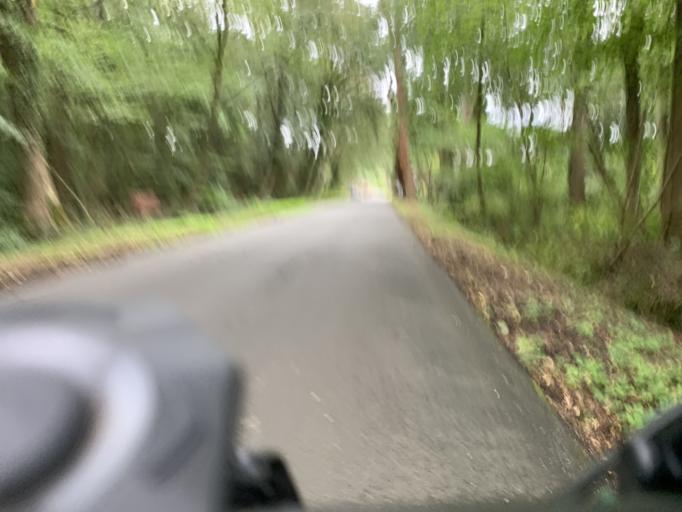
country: DE
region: Lower Saxony
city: Westerstede
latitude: 53.2349
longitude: 7.9398
